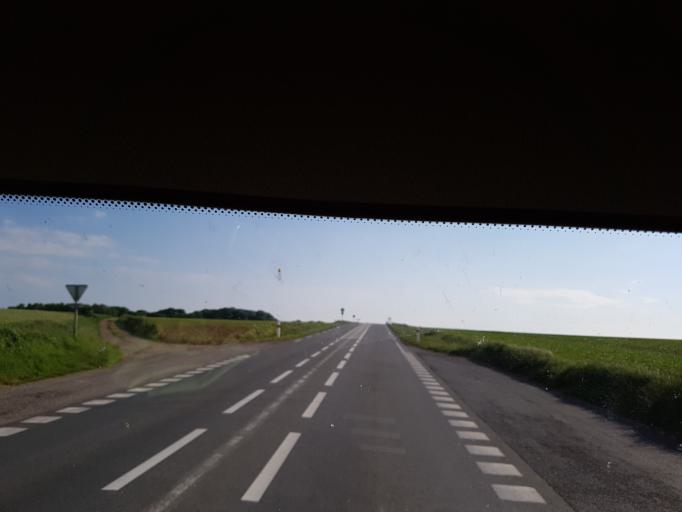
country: FR
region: Picardie
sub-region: Departement de la Somme
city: Crecy-en-Ponthieu
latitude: 50.2232
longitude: 1.9252
